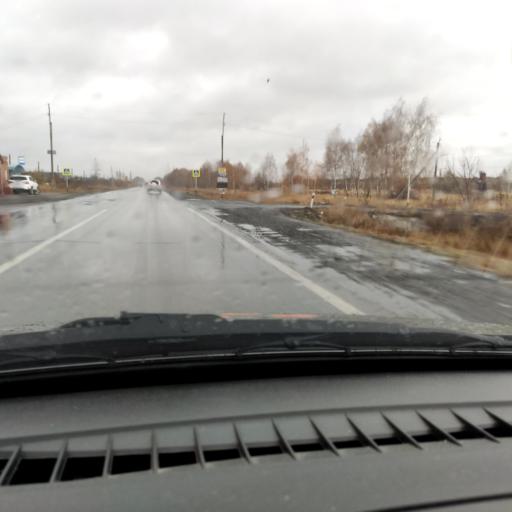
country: RU
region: Samara
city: Tol'yatti
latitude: 53.5787
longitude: 49.3371
